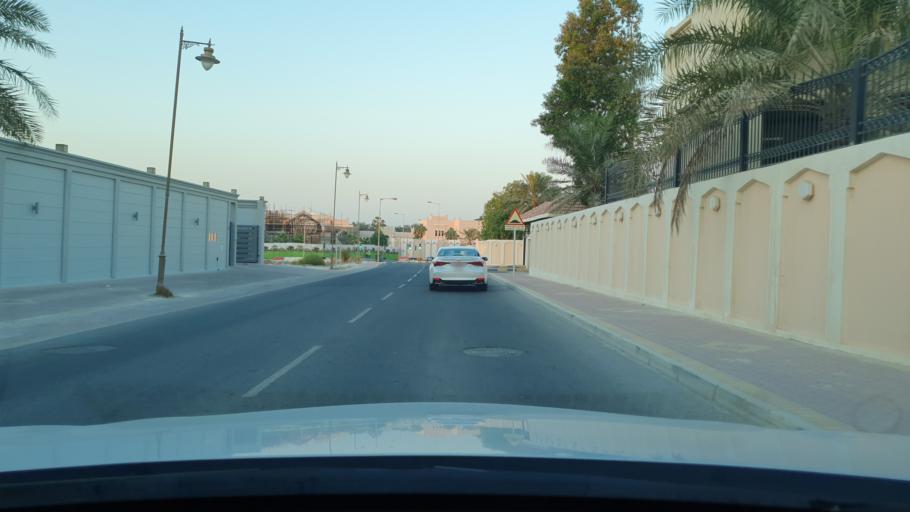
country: BH
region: Northern
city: Ar Rifa'
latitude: 26.1392
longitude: 50.5327
